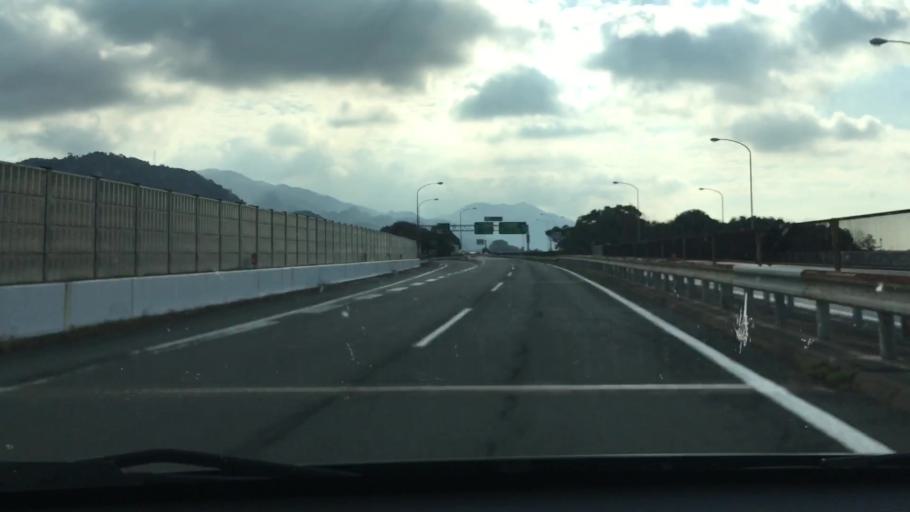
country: JP
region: Kumamoto
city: Yatsushiro
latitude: 32.5154
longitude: 130.6493
